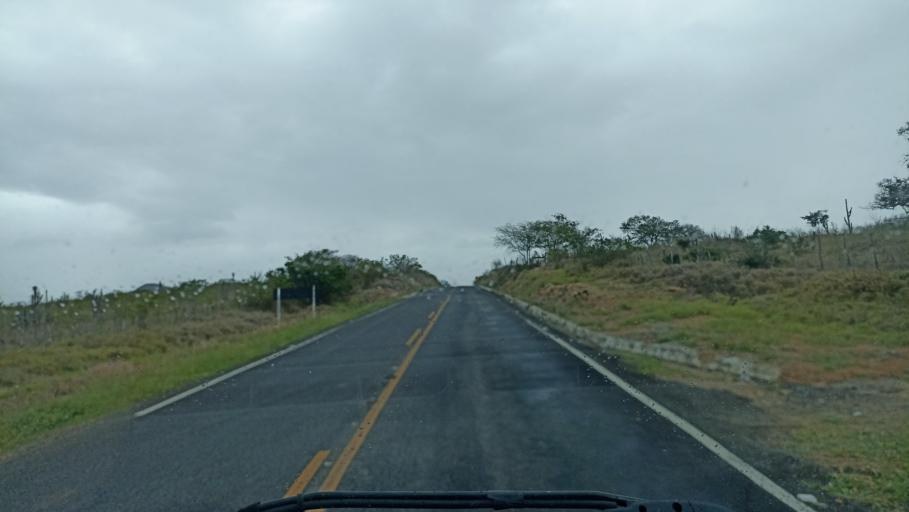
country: BR
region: Bahia
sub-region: Andarai
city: Vera Cruz
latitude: -13.0491
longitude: -40.7508
